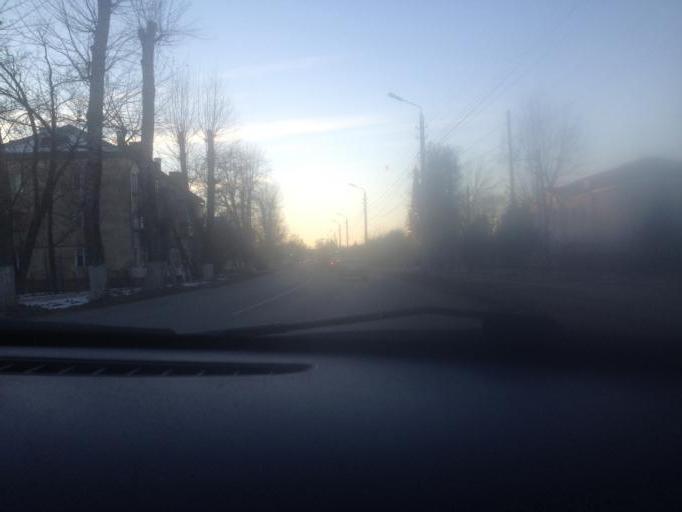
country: RU
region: Tula
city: Tula
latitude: 54.1955
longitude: 37.5574
